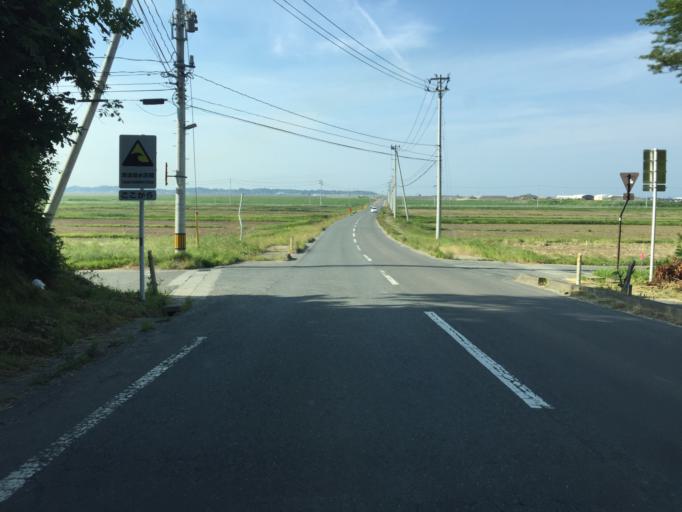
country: JP
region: Fukushima
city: Namie
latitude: 37.6767
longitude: 141.0031
